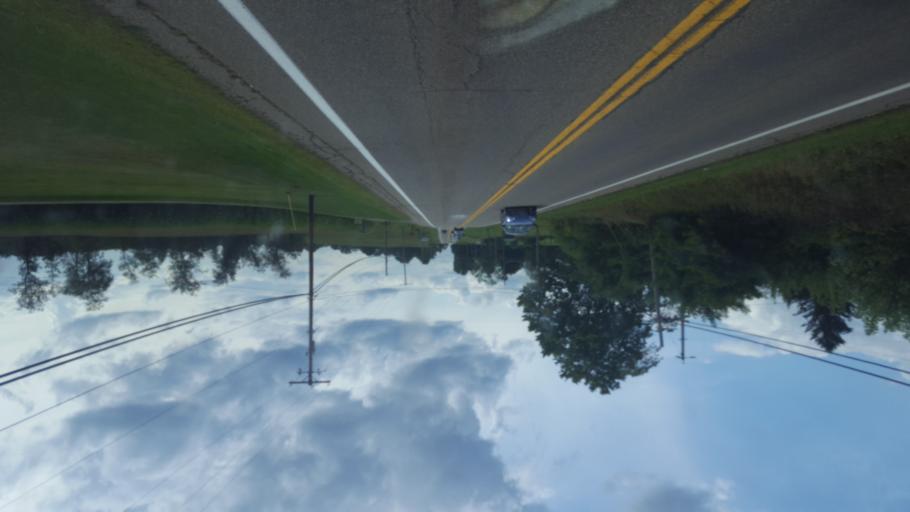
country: US
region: Ohio
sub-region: Portage County
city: Ravenna
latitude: 41.0504
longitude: -81.2478
